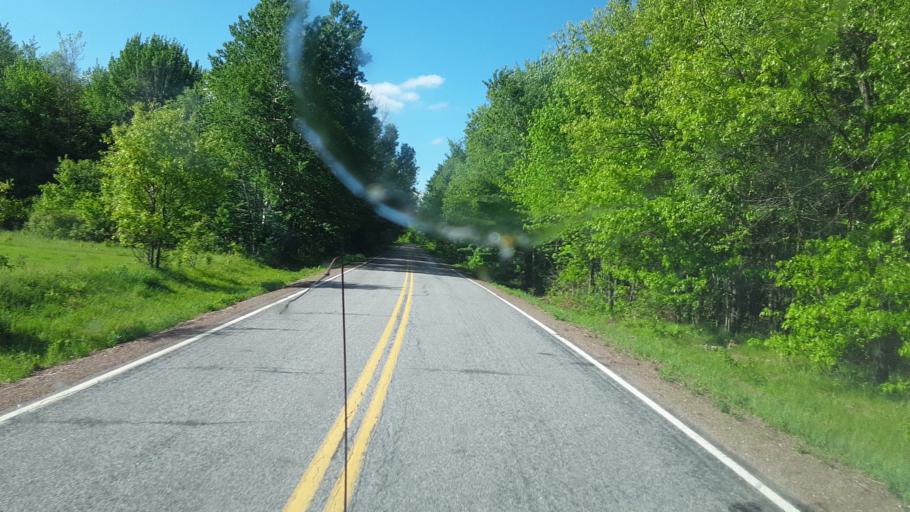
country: US
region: Wisconsin
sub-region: Wood County
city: Nekoosa
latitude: 44.3165
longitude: -90.1259
